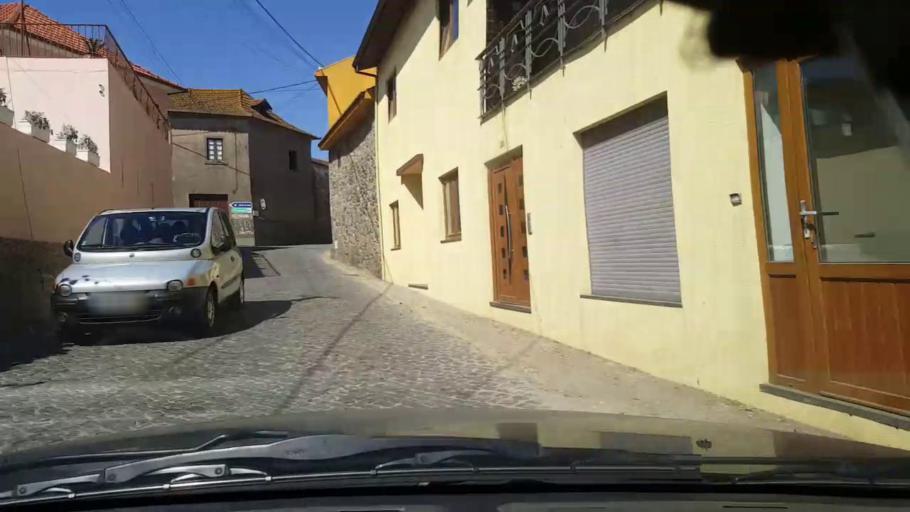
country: PT
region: Porto
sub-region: Matosinhos
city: Lavra
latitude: 41.2772
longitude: -8.7092
